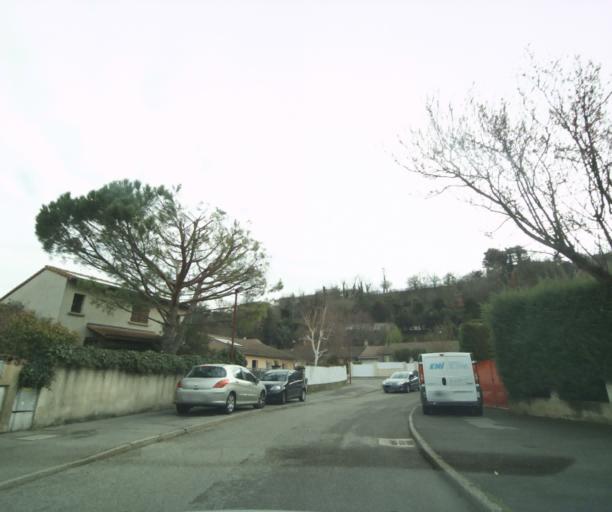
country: FR
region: Rhone-Alpes
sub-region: Departement de la Drome
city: Bourg-les-Valence
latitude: 44.9469
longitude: 4.9014
